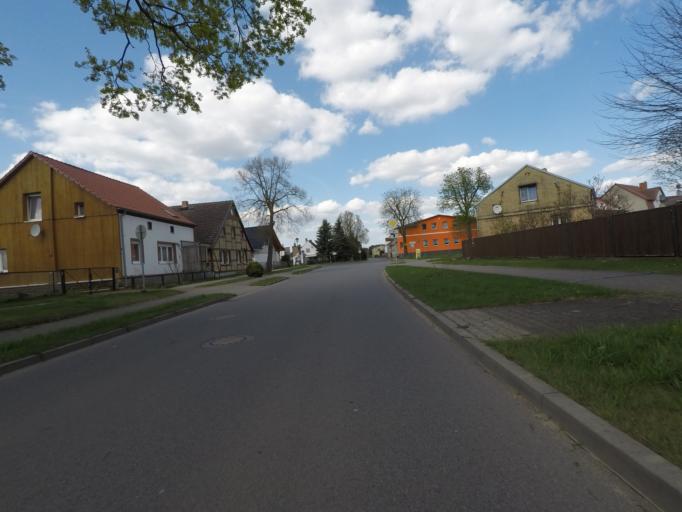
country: DE
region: Brandenburg
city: Melchow
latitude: 52.8525
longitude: 13.6820
